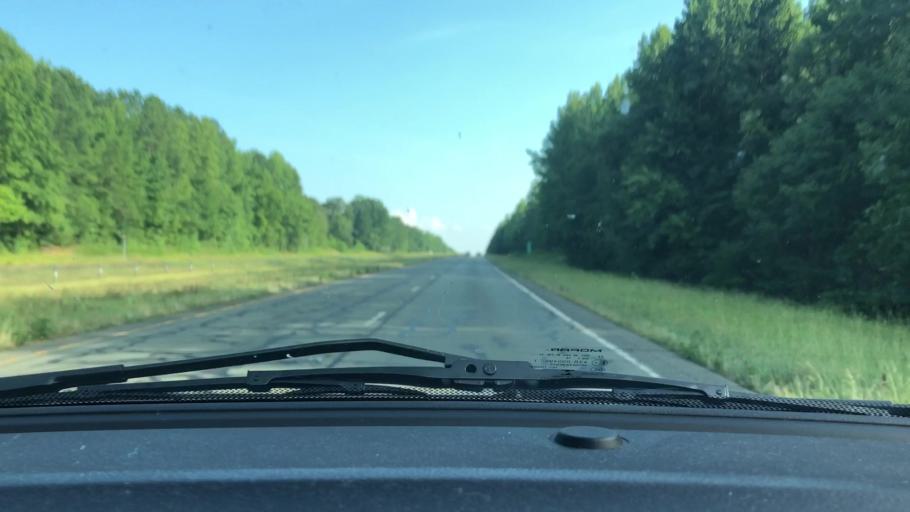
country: US
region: North Carolina
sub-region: Chatham County
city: Siler City
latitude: 35.7217
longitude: -79.4299
